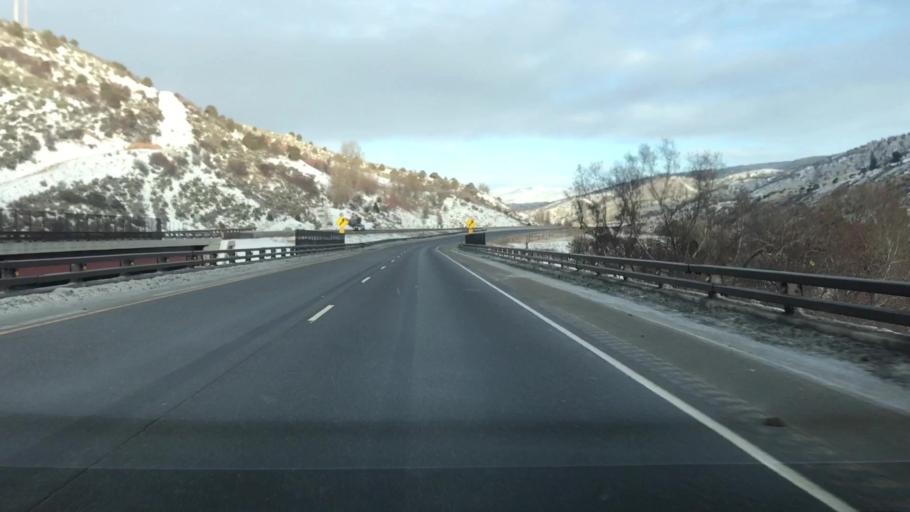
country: US
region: Colorado
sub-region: Eagle County
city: Edwards
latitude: 39.6741
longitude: -106.6468
